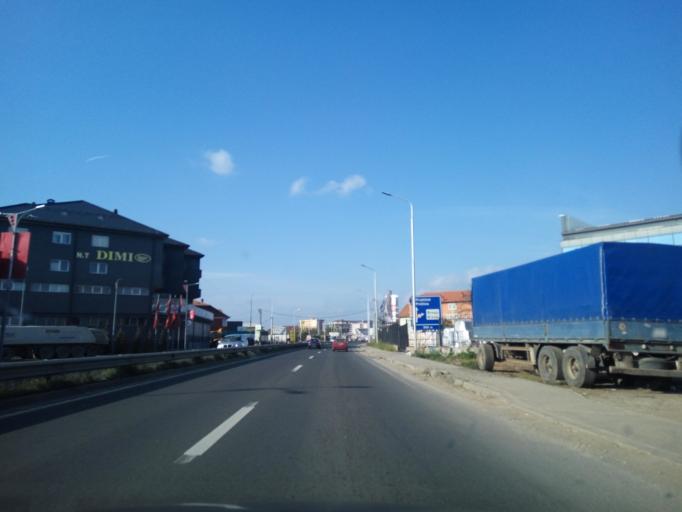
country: XK
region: Pristina
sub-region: Kosovo Polje
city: Kosovo Polje
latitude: 42.6263
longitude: 21.0877
